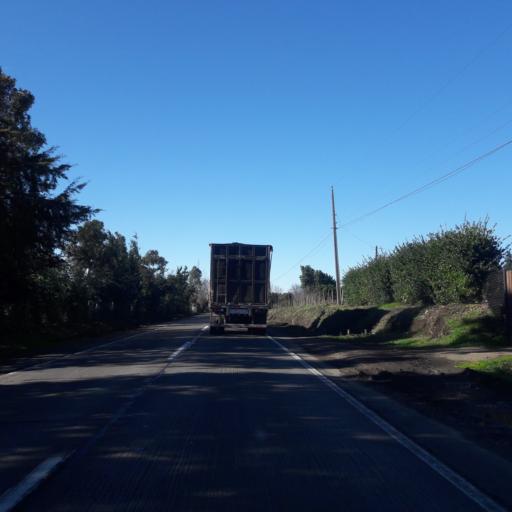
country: CL
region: Araucania
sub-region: Provincia de Malleco
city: Angol
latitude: -37.7797
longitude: -72.5357
